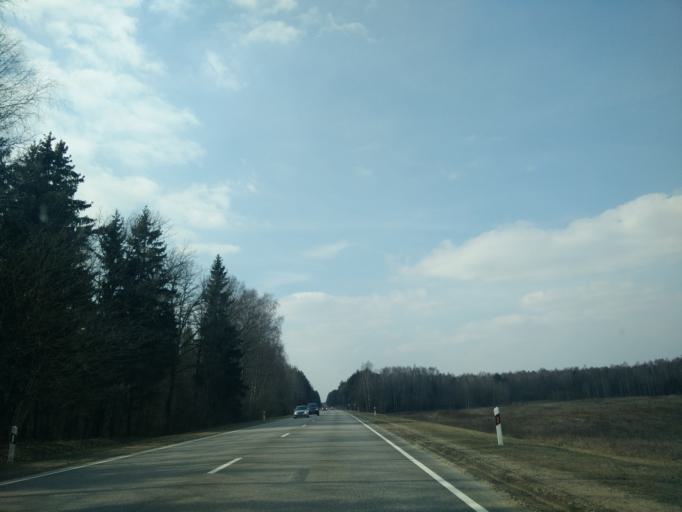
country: LT
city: Lentvaris
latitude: 54.6229
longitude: 25.0316
